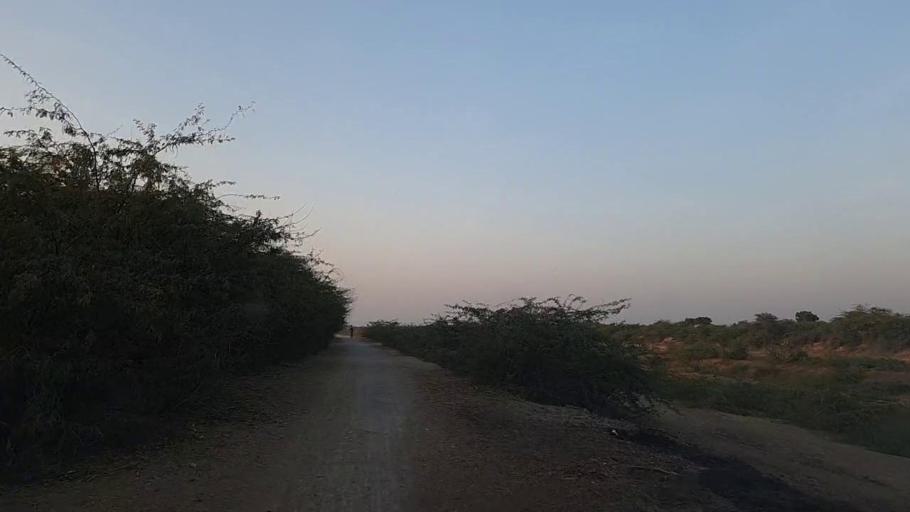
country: PK
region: Sindh
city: Naukot
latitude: 24.9506
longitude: 69.4285
